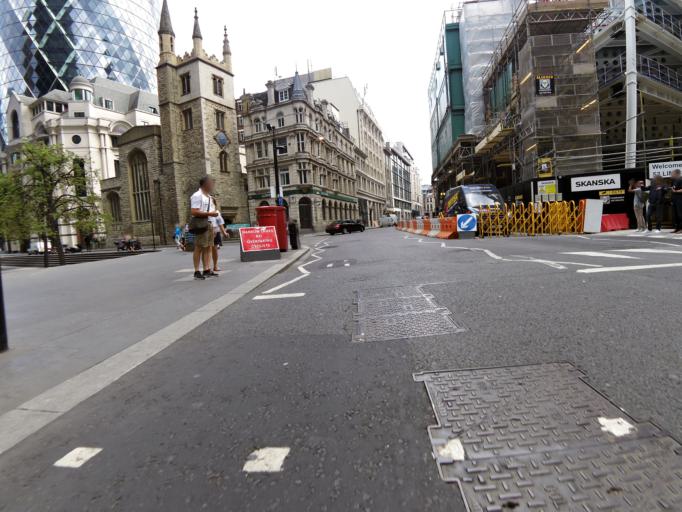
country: GB
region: England
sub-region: Greater London
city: City of London
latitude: 51.5137
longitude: -0.0814
